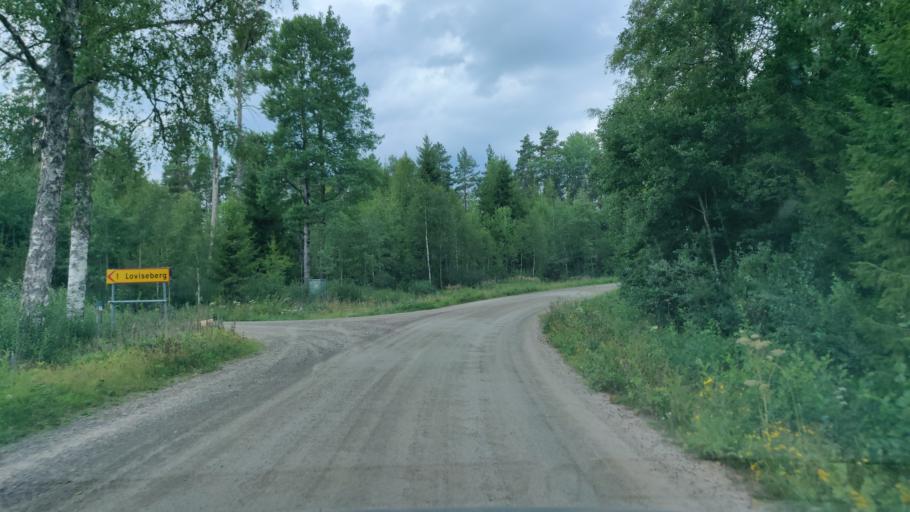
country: SE
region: Vaermland
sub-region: Munkfors Kommun
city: Munkfors
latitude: 59.9597
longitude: 13.4929
